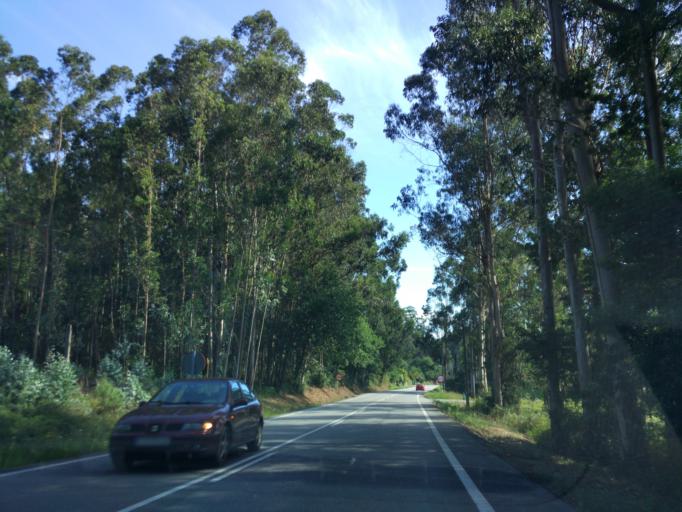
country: ES
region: Galicia
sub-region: Provincia da Coruna
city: Padron
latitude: 42.7222
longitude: -8.6799
